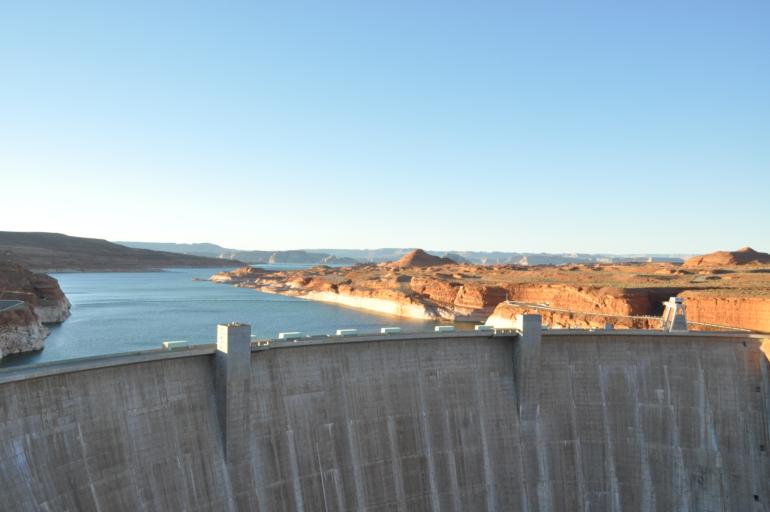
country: US
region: Arizona
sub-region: Coconino County
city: Page
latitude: 36.9353
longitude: -111.4860
